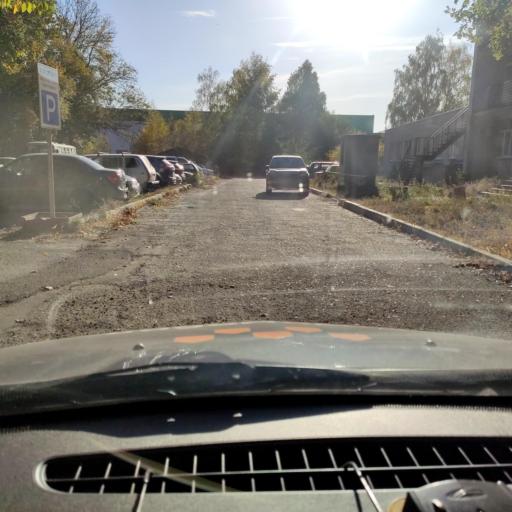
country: RU
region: Voronezj
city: Podgornoye
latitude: 51.8089
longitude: 39.2231
